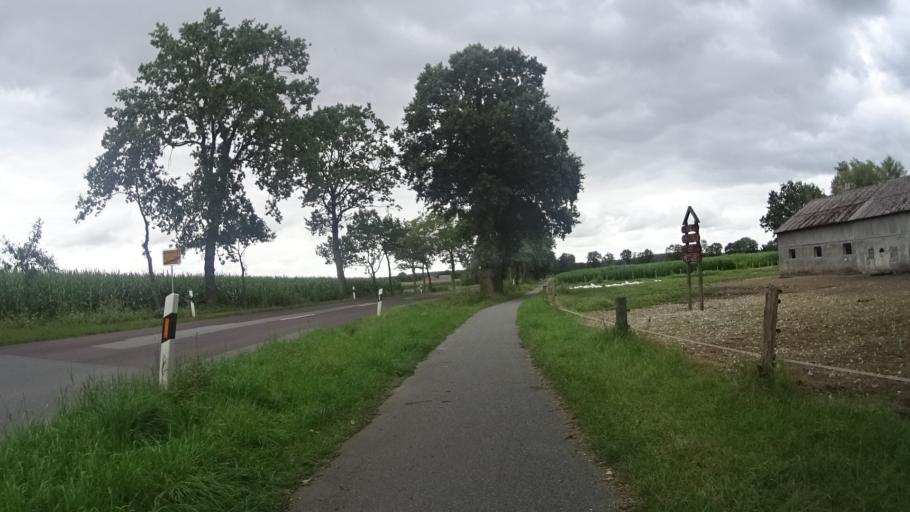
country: DE
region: Lower Saxony
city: Kuhrstedt
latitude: 53.6001
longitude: 8.8124
